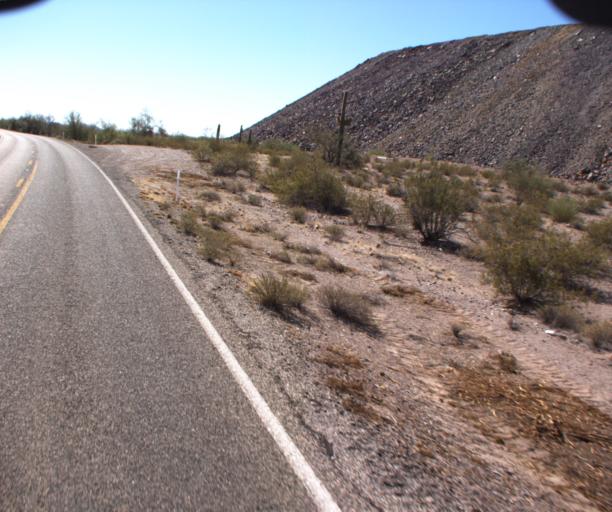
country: US
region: Arizona
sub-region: Pima County
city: Ajo
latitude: 32.3584
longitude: -112.8309
